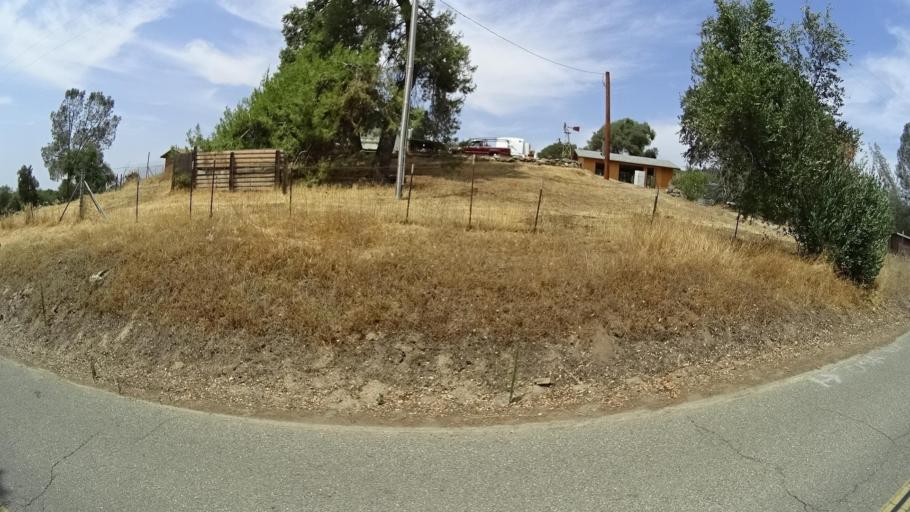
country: US
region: California
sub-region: Madera County
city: Ahwahnee
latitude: 37.4196
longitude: -119.8177
